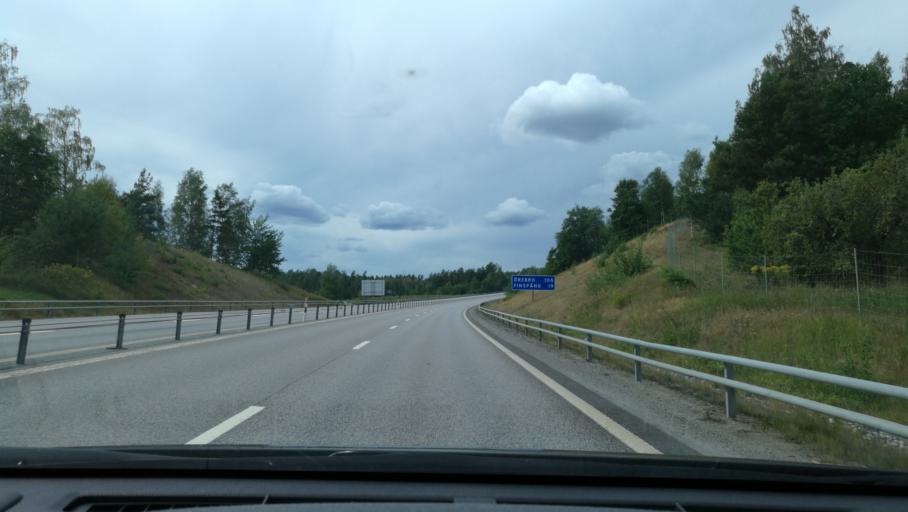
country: SE
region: OEstergoetland
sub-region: Norrkopings Kommun
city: Svartinge
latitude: 58.6479
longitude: 16.0552
